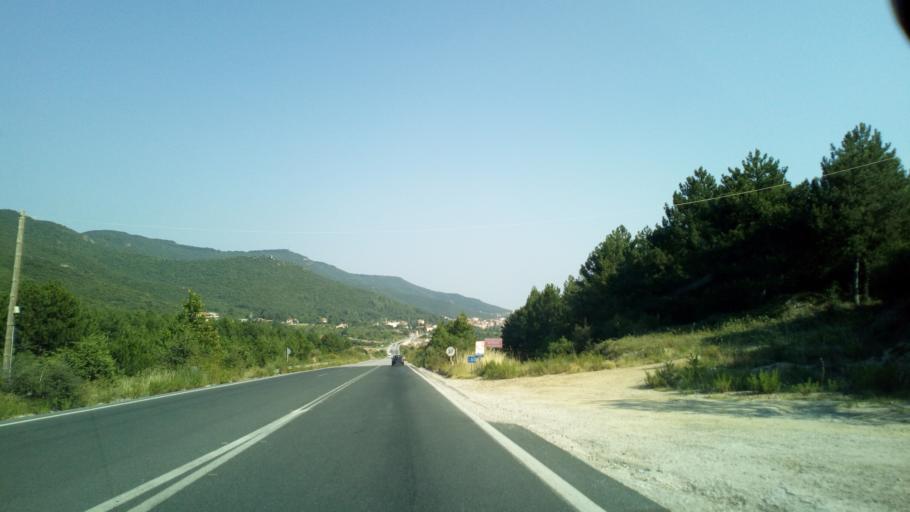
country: GR
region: Central Macedonia
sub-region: Nomos Chalkidikis
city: Polygyros
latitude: 40.3963
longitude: 23.4276
